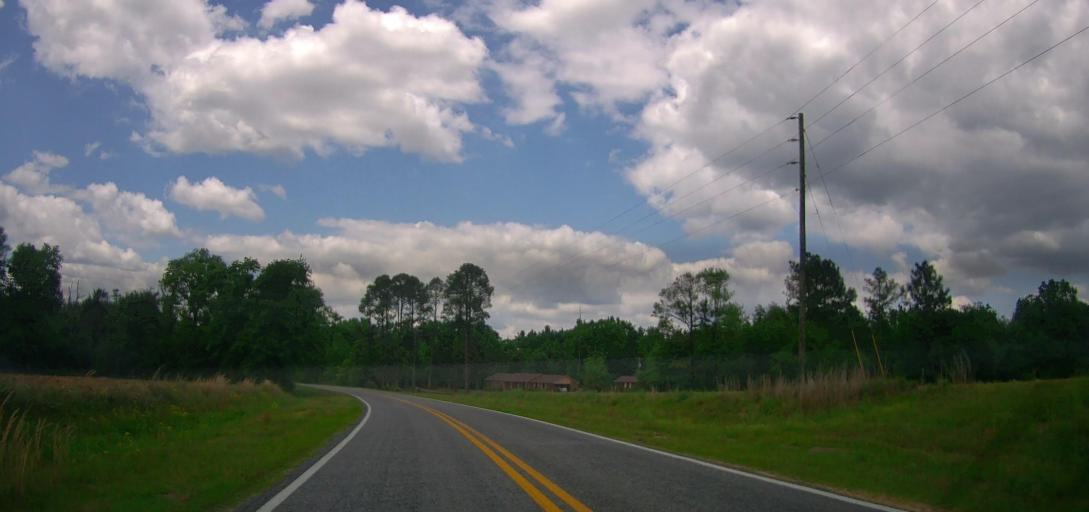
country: US
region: Georgia
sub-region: Laurens County
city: East Dublin
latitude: 32.5387
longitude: -82.8104
